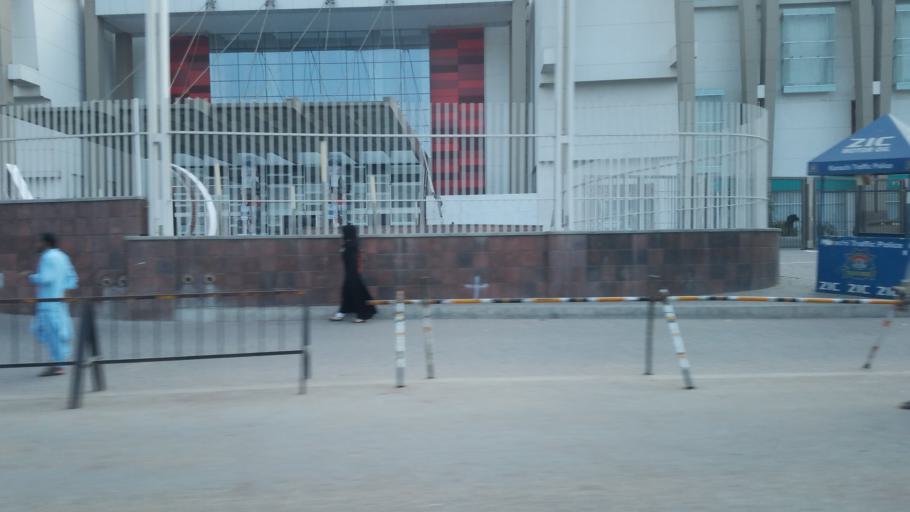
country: PK
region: Sindh
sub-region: Karachi District
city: Karachi
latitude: 24.9324
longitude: 67.0860
